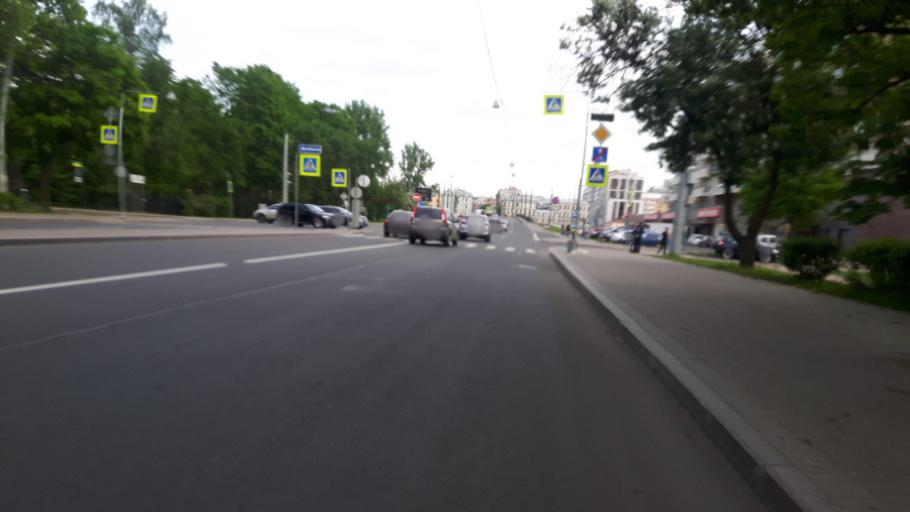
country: RU
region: Leningrad
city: Krestovskiy ostrov
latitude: 59.9688
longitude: 30.2770
